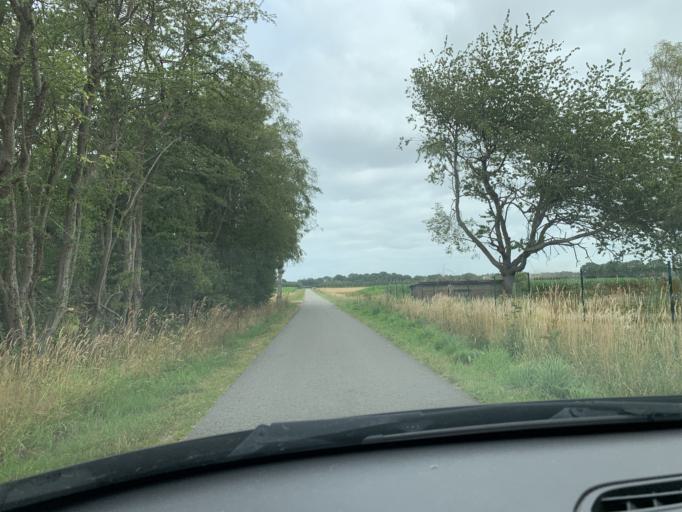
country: DE
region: Lower Saxony
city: Bad Zwischenahn
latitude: 53.2283
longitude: 7.9746
